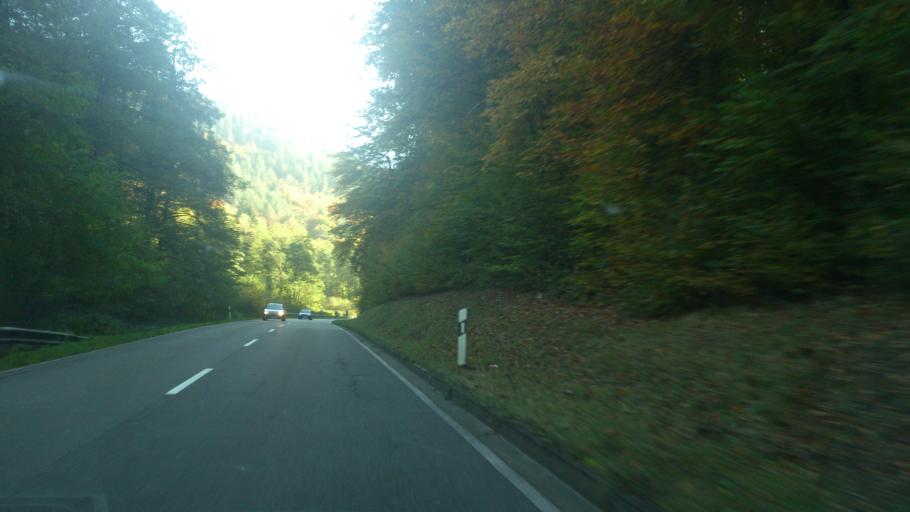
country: DE
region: Rheinland-Pfalz
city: Frankeneck
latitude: 49.3635
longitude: 8.0284
